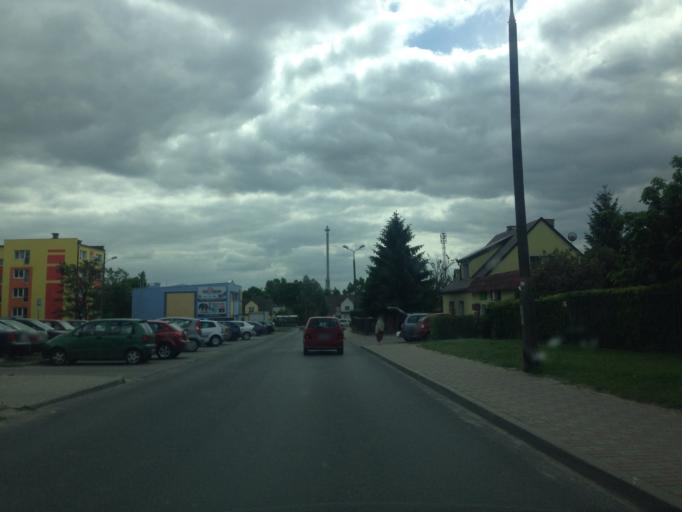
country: PL
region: Kujawsko-Pomorskie
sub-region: Powiat swiecki
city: Swiecie
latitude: 53.4064
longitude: 18.4242
